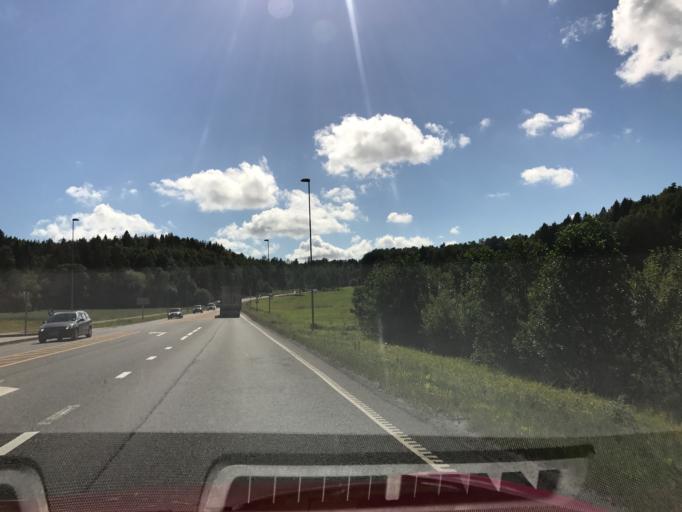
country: NO
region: Telemark
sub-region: Bamble
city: Langesund
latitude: 58.9882
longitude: 9.6281
